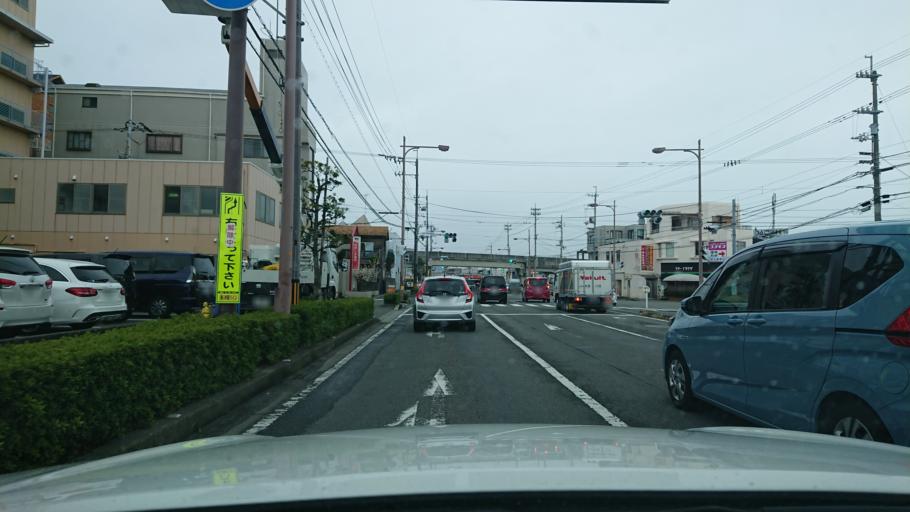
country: JP
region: Tokushima
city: Tokushima-shi
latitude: 34.0862
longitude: 134.5317
